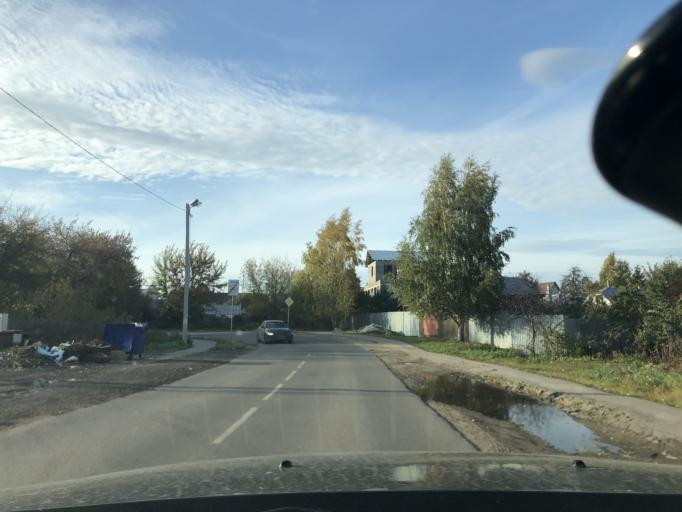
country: RU
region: Tula
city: Tula
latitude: 54.1894
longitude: 37.6331
